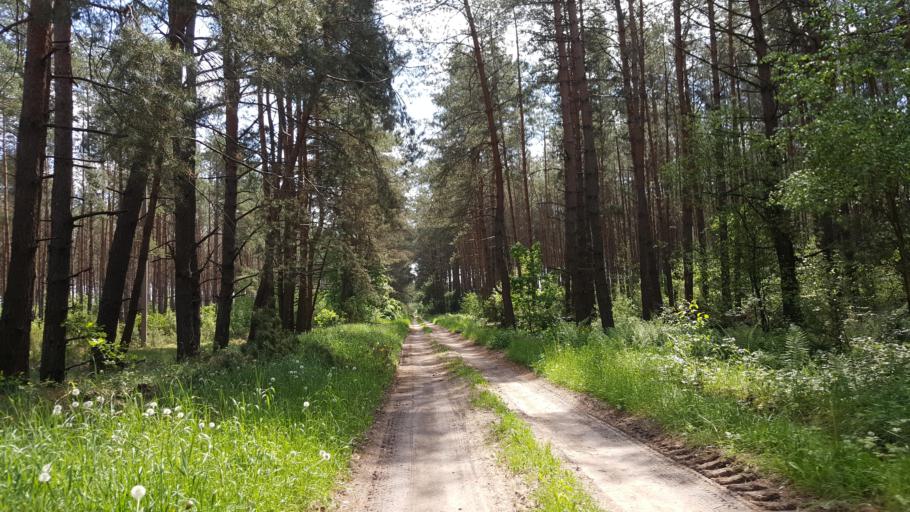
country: BY
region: Brest
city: Kamyanyets
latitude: 52.3945
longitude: 23.8668
